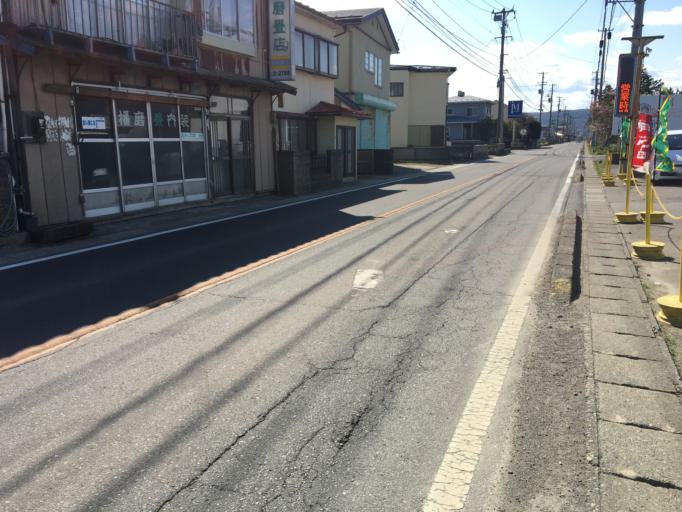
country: JP
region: Aomori
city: Hachinohe
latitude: 40.2080
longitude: 141.7934
